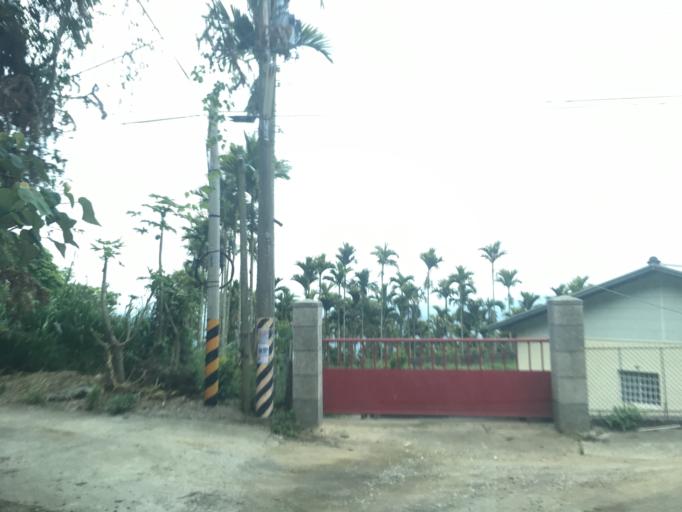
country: TW
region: Taiwan
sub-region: Nantou
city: Puli
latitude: 23.9648
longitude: 120.8412
